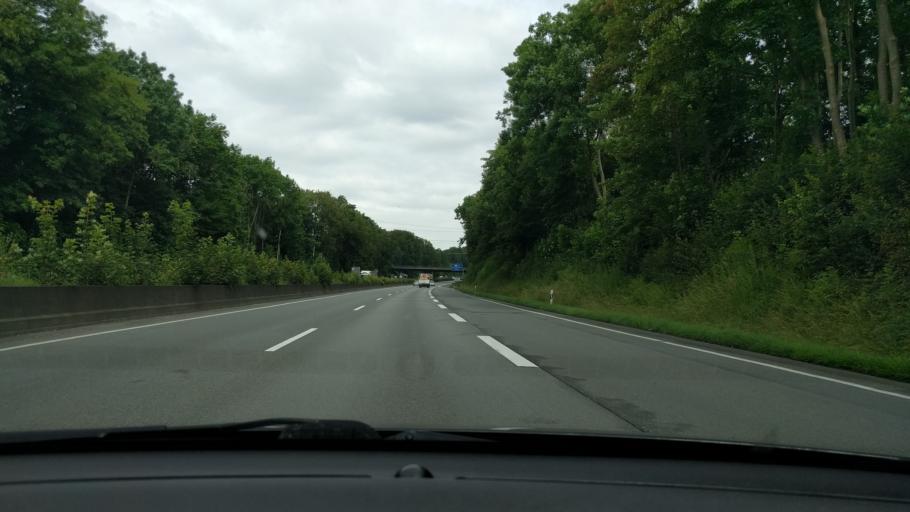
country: DE
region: North Rhine-Westphalia
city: Castrop-Rauxel
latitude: 51.5386
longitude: 7.3668
